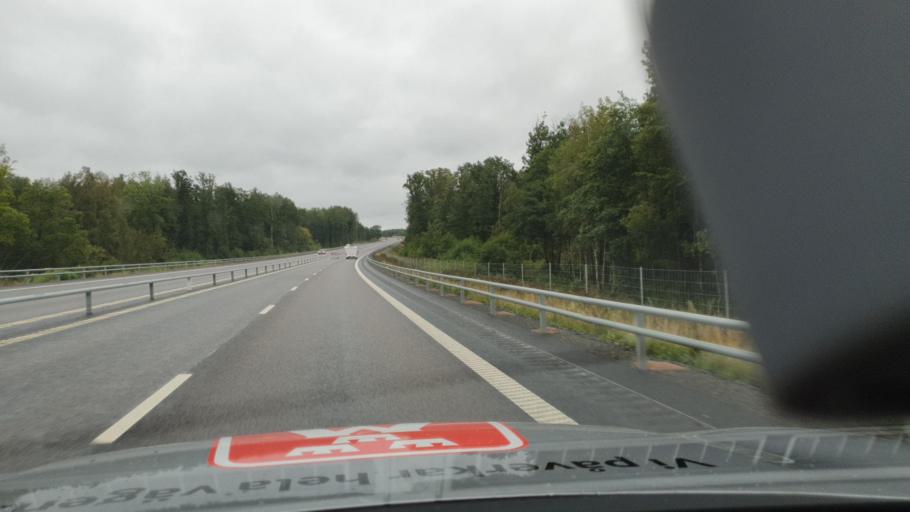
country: SE
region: Skane
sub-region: Hassleholms Kommun
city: Vinslov
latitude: 55.9495
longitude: 13.8999
